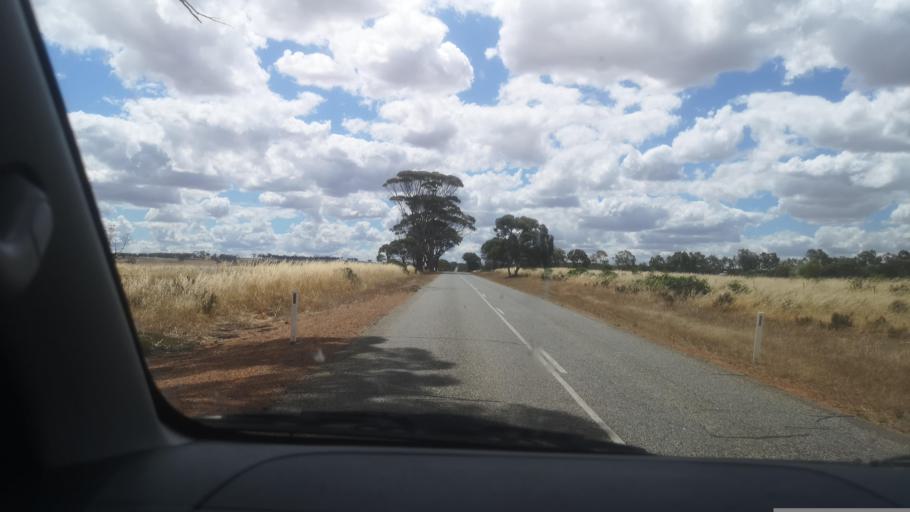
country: AU
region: Western Australia
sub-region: Beverley
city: Beverley
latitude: -31.9757
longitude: 117.0805
